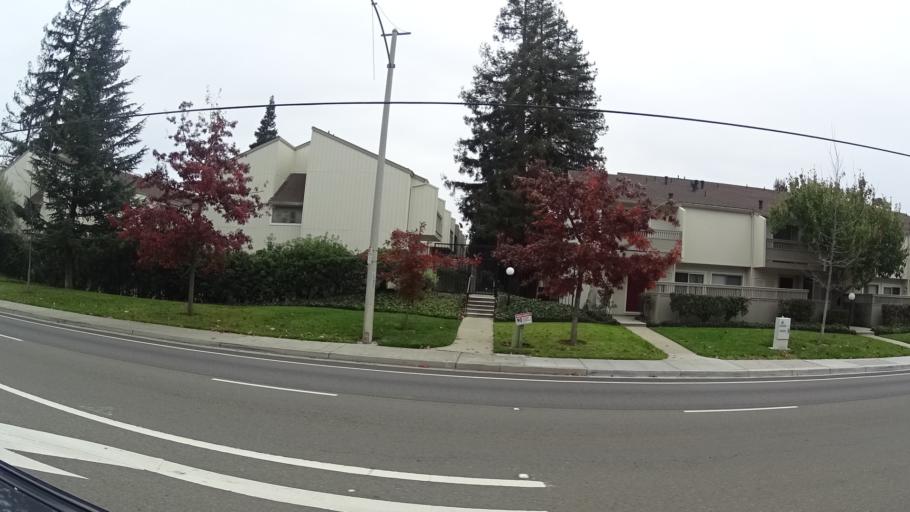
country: US
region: California
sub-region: Santa Clara County
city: Sunnyvale
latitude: 37.3660
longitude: -122.0236
